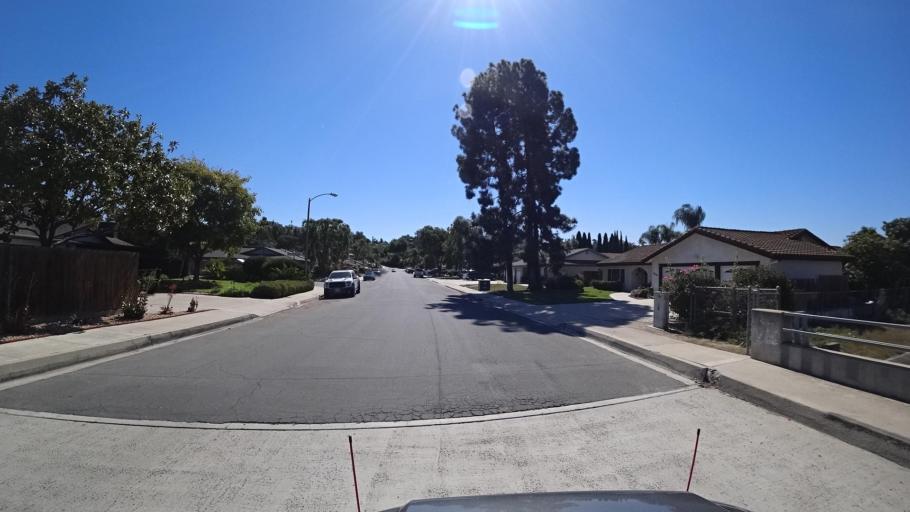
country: US
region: California
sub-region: San Diego County
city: Bonita
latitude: 32.6674
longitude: -117.0218
